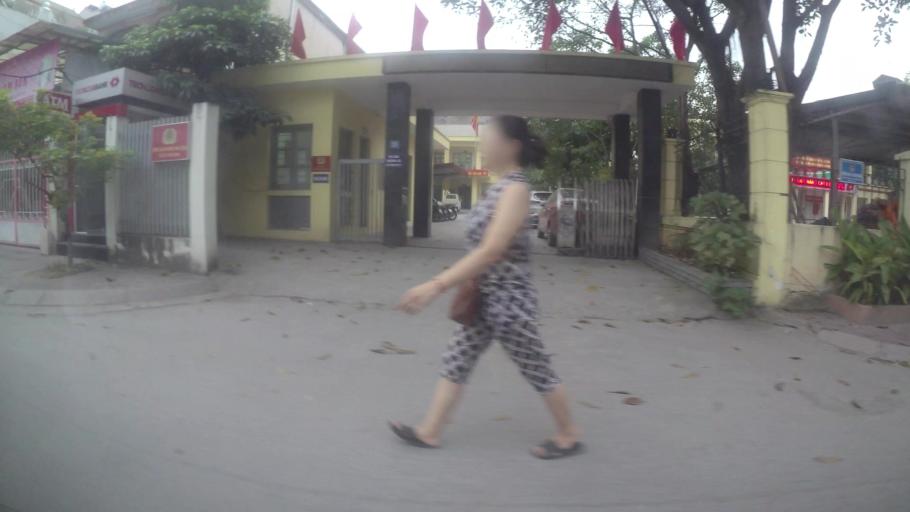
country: VN
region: Ha Noi
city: Cau Dien
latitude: 21.0356
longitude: 105.7788
